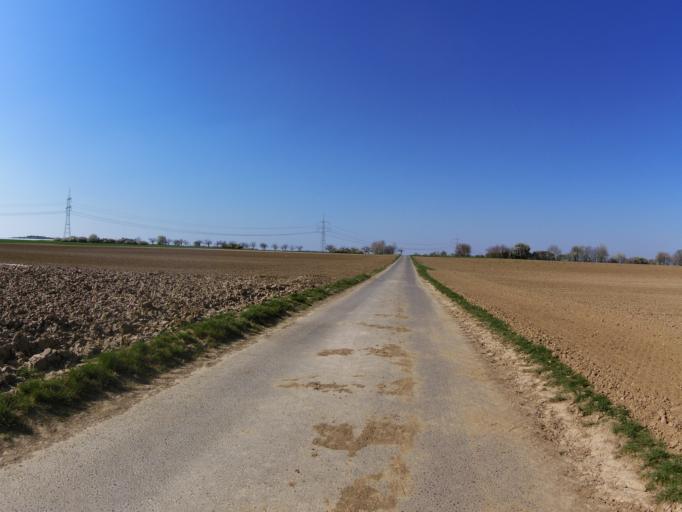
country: DE
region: Bavaria
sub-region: Regierungsbezirk Unterfranken
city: Biebelried
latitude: 49.8187
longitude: 10.0927
